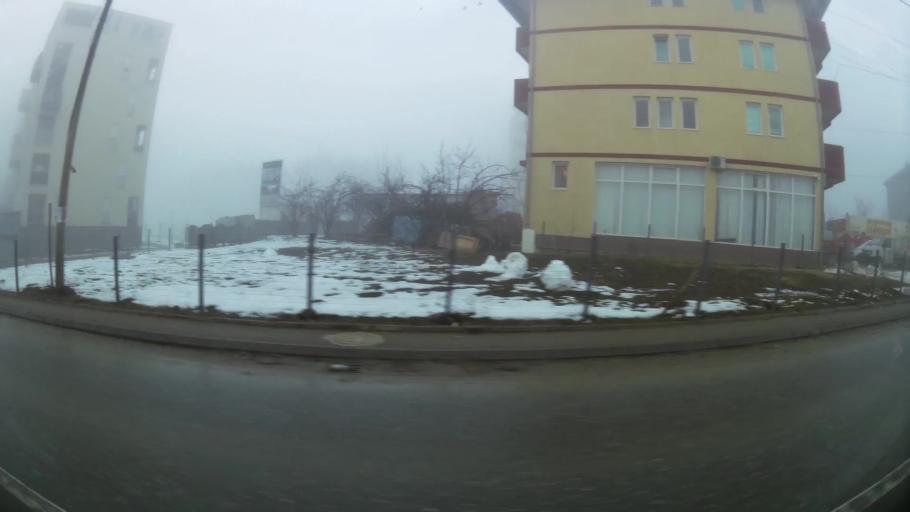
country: XK
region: Pristina
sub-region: Komuna e Prishtines
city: Pristina
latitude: 42.6591
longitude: 21.1416
